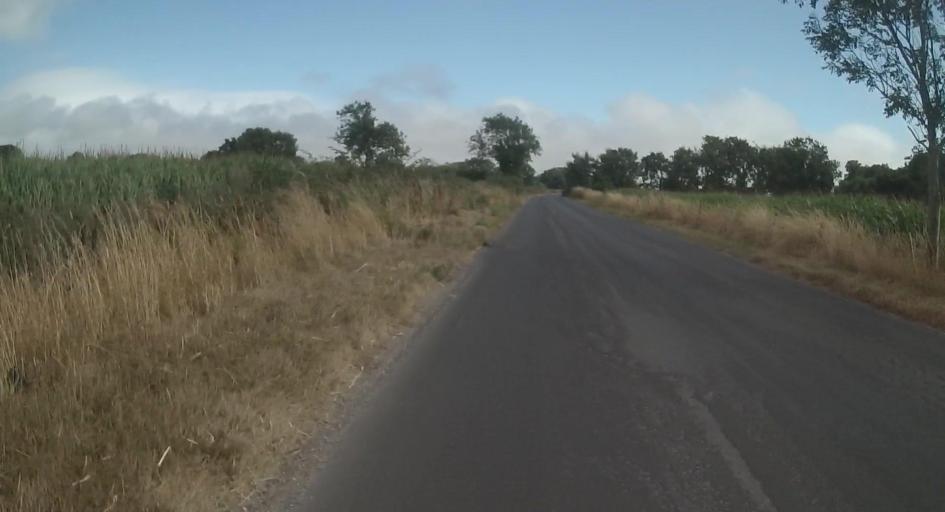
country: GB
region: England
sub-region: Dorset
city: Bovington Camp
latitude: 50.6988
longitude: -2.2742
